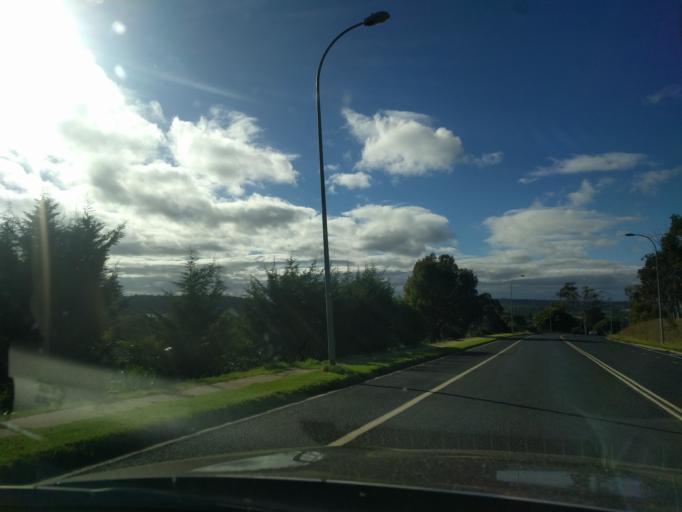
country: AU
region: New South Wales
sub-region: Armidale Dumaresq
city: Armidale
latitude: -30.4966
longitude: 151.6702
